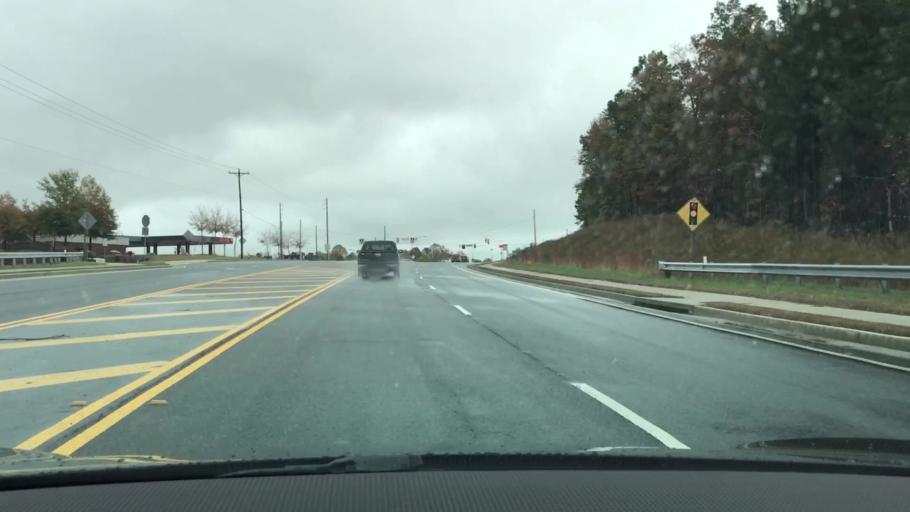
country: US
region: Georgia
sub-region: Gwinnett County
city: Buford
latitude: 34.1500
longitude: -83.9754
